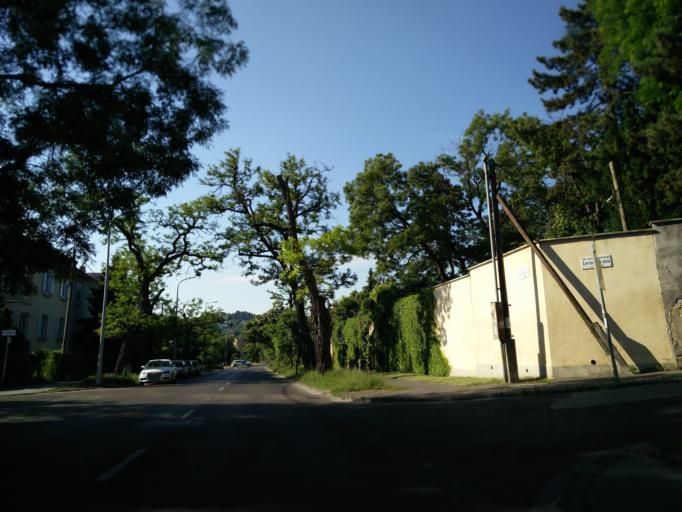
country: HU
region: Budapest
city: Budapest XII. keruelet
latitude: 47.4943
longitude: 19.0115
